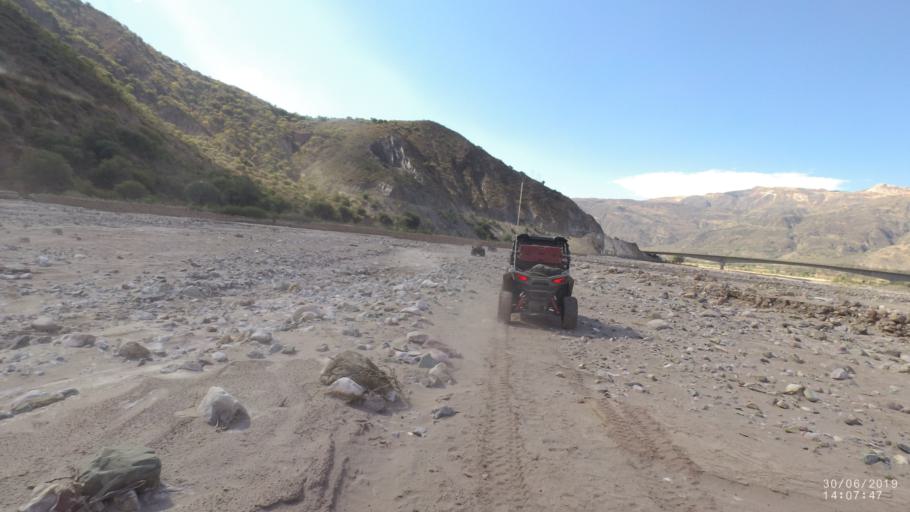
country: BO
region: Cochabamba
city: Irpa Irpa
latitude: -17.8010
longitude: -66.3543
